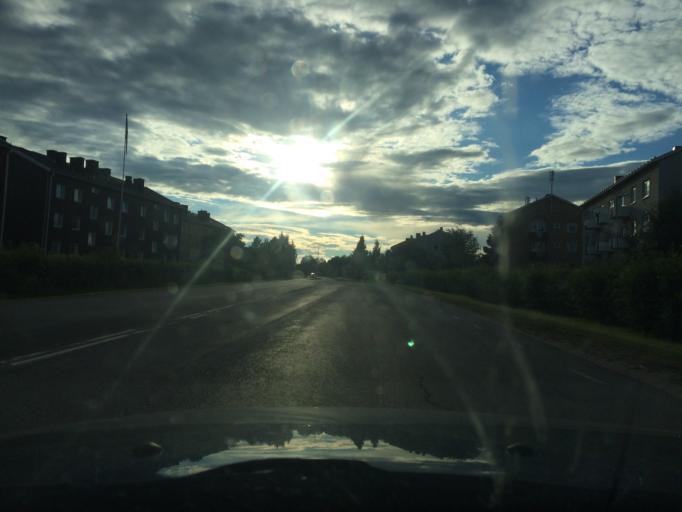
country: SE
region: Norrbotten
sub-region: Pitea Kommun
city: Pitea
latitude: 65.3216
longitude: 21.4703
